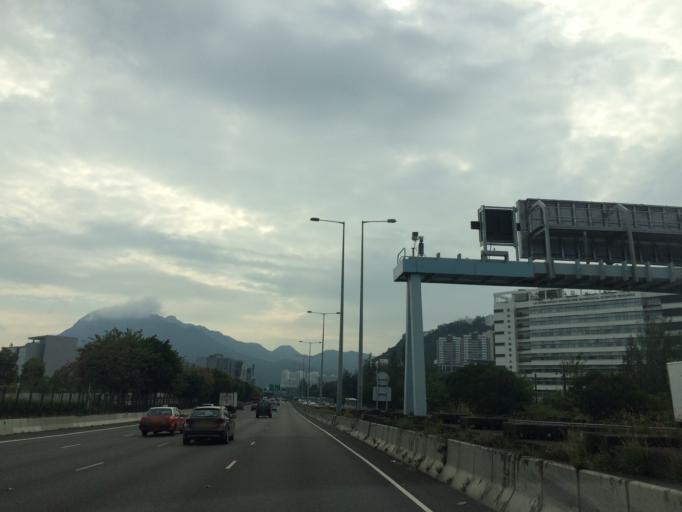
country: HK
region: Tai Po
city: Tai Po
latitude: 22.4296
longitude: 114.2029
